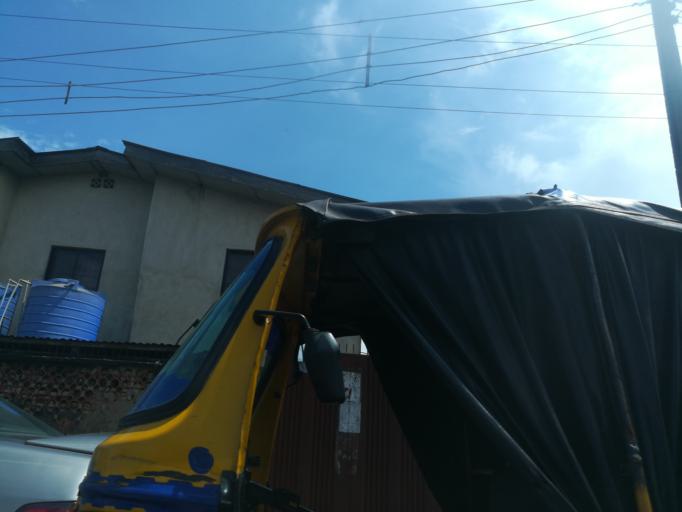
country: NG
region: Lagos
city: Agege
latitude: 6.6220
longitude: 3.3293
